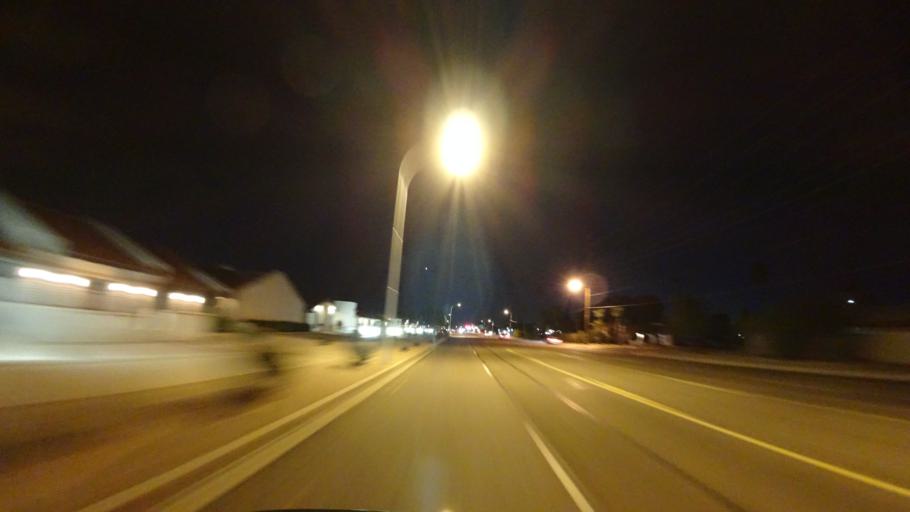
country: US
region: Arizona
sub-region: Maricopa County
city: Tempe
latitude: 33.3929
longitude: -111.8861
